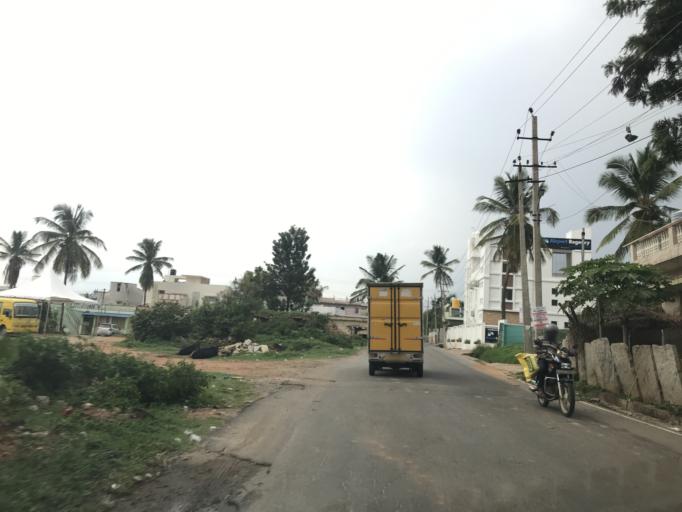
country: IN
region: Karnataka
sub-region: Bangalore Rural
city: Devanhalli
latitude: 13.1776
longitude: 77.6531
